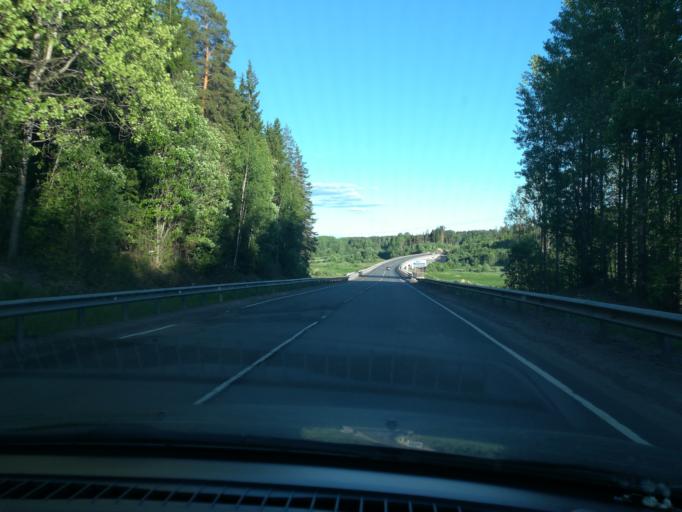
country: RU
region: Leningrad
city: Lesogorskiy
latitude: 61.0142
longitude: 28.9144
